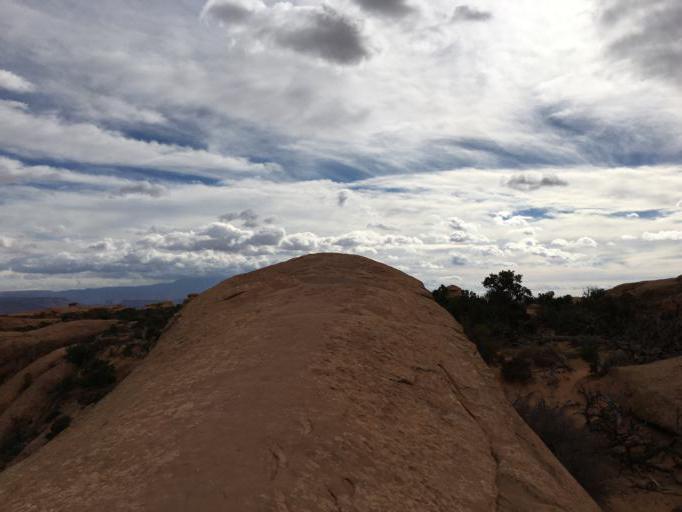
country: US
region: Utah
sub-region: Grand County
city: Moab
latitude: 38.7967
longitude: -109.6157
